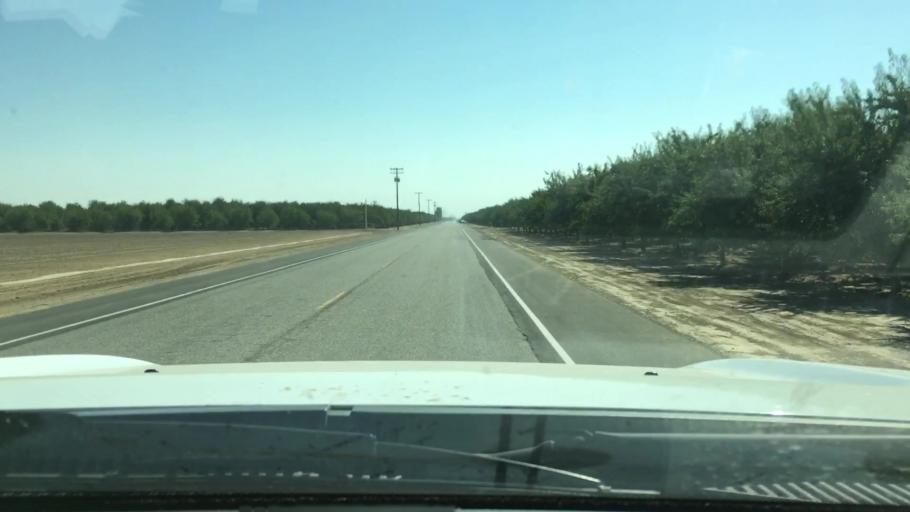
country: US
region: California
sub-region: Kern County
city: Wasco
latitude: 35.5578
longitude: -119.4317
